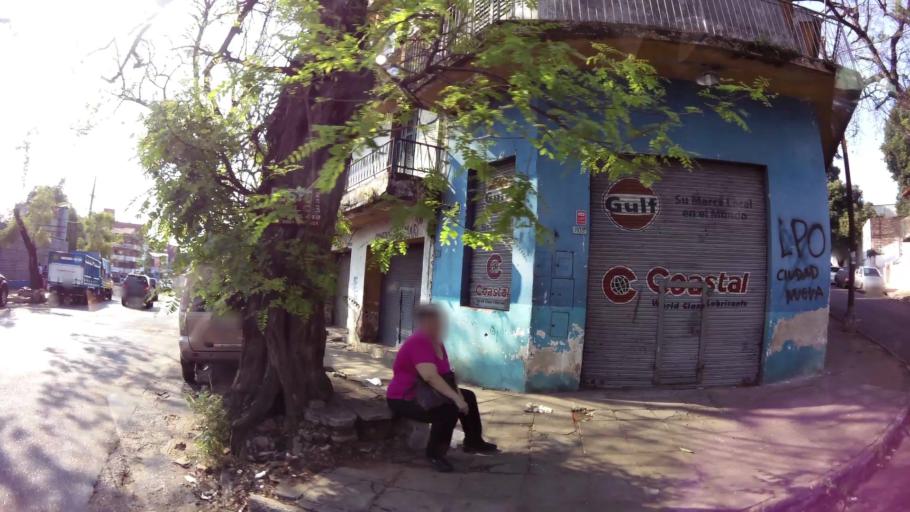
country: PY
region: Asuncion
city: Asuncion
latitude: -25.3018
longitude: -57.6201
